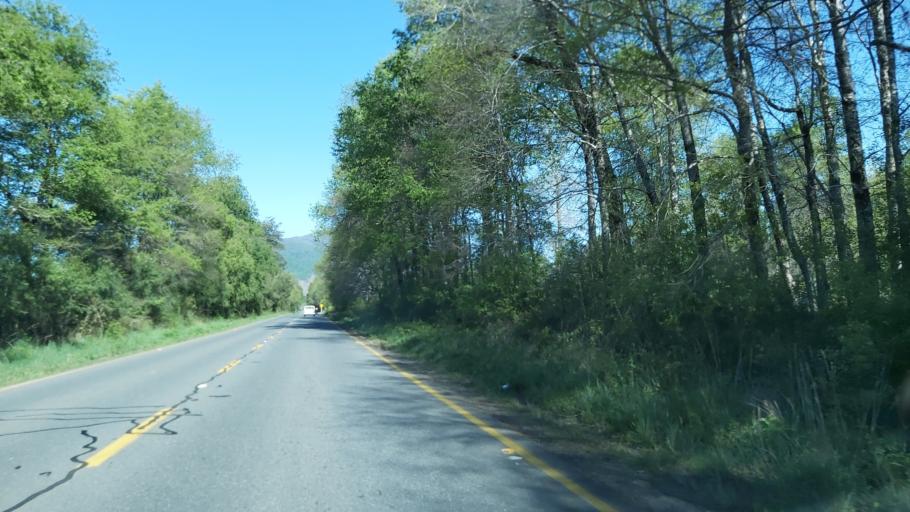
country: CL
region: Araucania
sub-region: Provincia de Cautin
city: Vilcun
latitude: -38.4864
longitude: -71.8354
